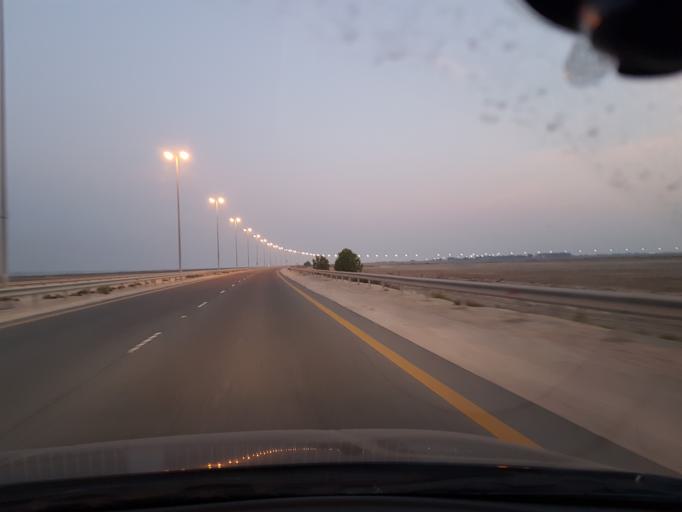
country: BH
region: Central Governorate
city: Dar Kulayb
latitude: 26.0083
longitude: 50.4844
